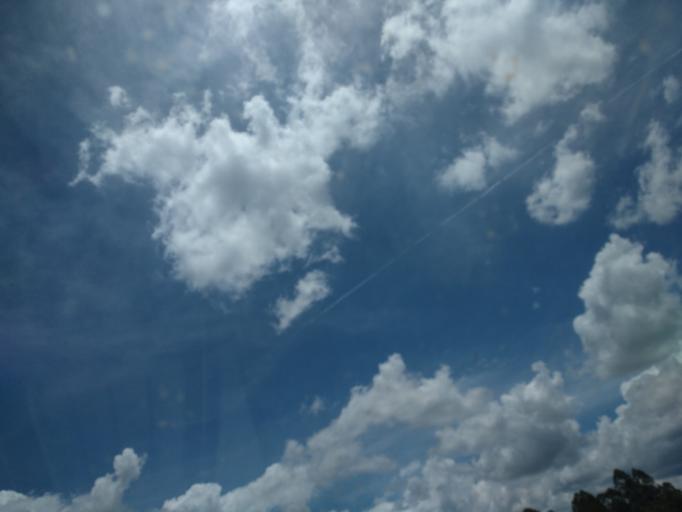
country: BR
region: Minas Gerais
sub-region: Tiradentes
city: Tiradentes
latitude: -20.9086
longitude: -44.2781
